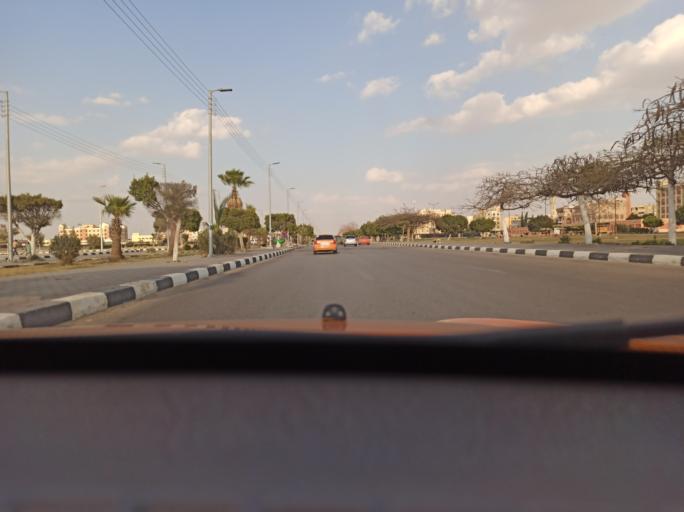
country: EG
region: Al Isma'iliyah
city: Ismailia
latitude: 30.6198
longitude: 32.2785
